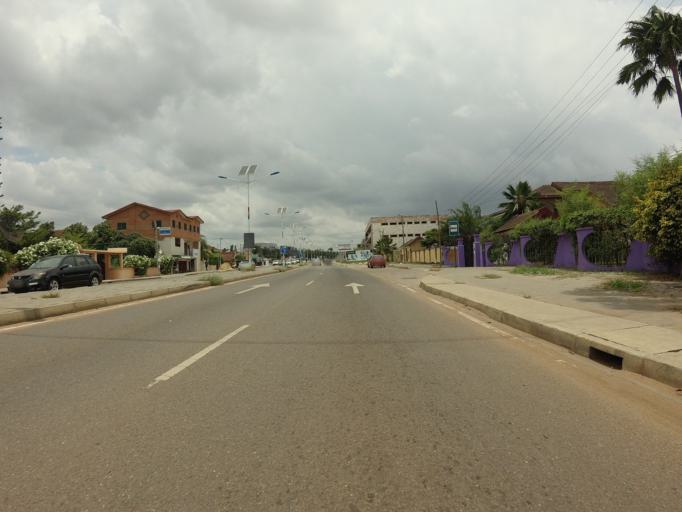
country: GH
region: Greater Accra
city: Medina Estates
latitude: 5.6528
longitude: -0.1507
